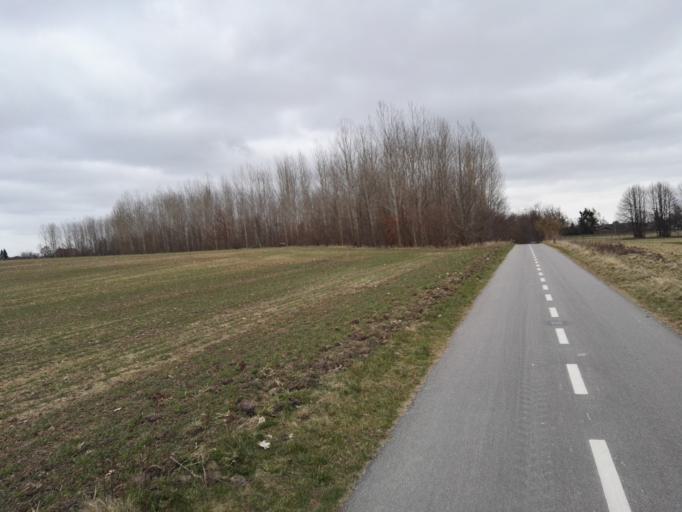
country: DK
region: Capital Region
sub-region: Ballerup Kommune
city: Ballerup
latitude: 55.7143
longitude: 12.3798
